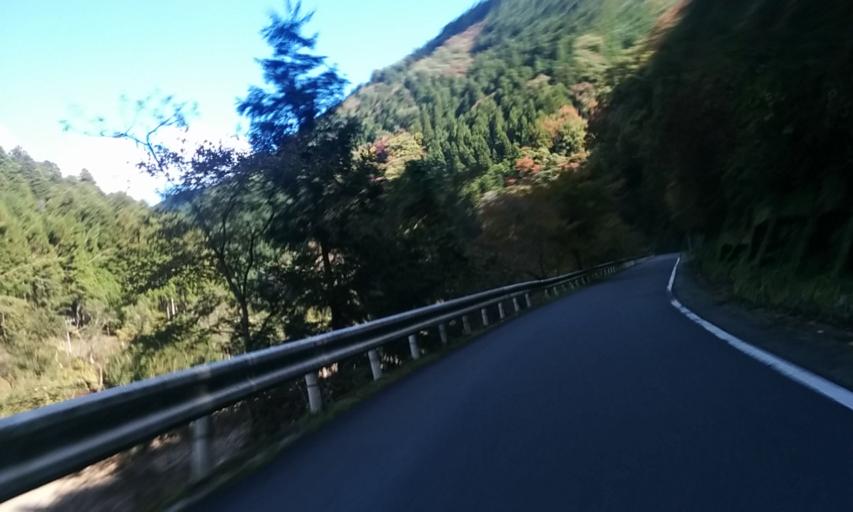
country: JP
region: Kyoto
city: Kameoka
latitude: 35.1313
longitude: 135.5723
